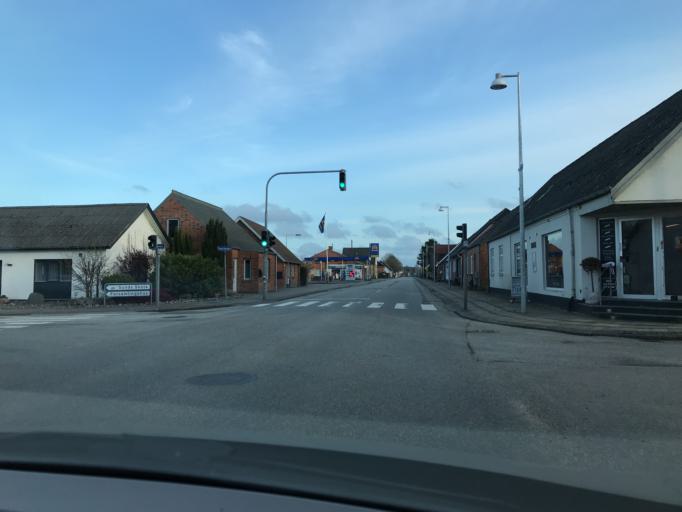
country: DK
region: Central Jutland
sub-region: Herning Kommune
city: Sunds
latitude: 56.2030
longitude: 9.0169
